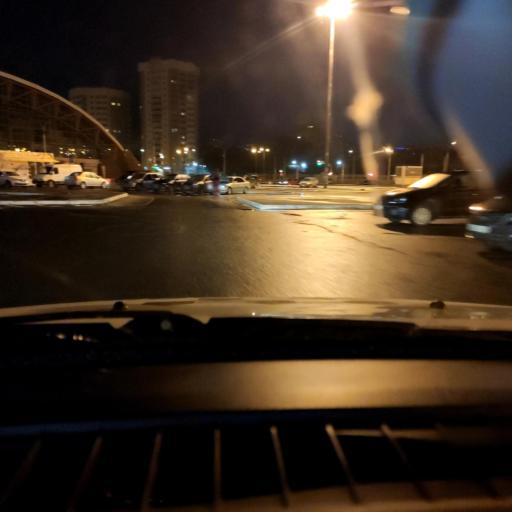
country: RU
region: Sverdlovsk
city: Yekaterinburg
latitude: 56.7971
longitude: 60.6298
